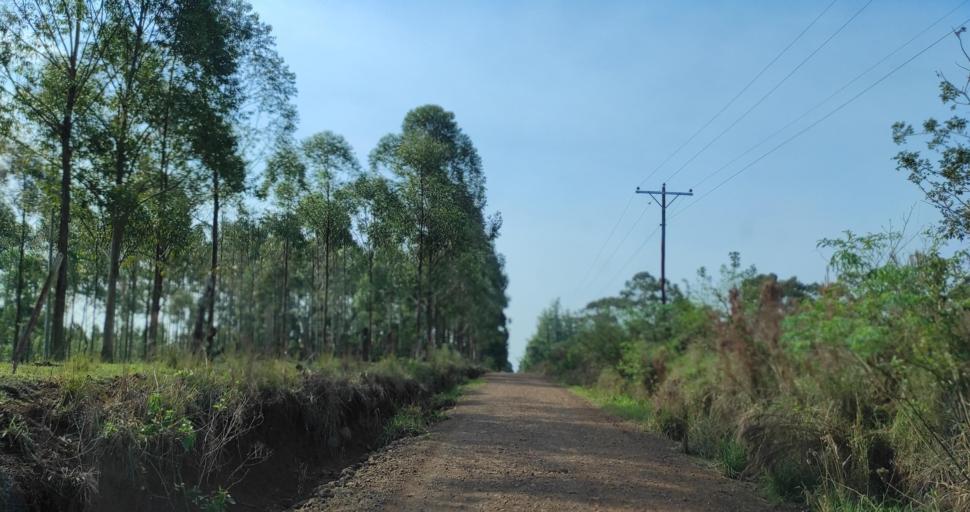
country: AR
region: Misiones
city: Capiovi
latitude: -26.8859
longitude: -55.0486
